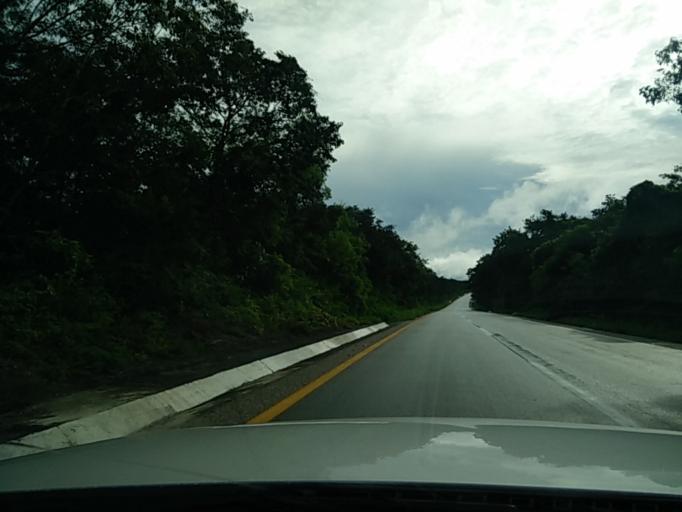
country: MX
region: Yucatan
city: Tunkas
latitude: 20.7654
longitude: -88.8010
